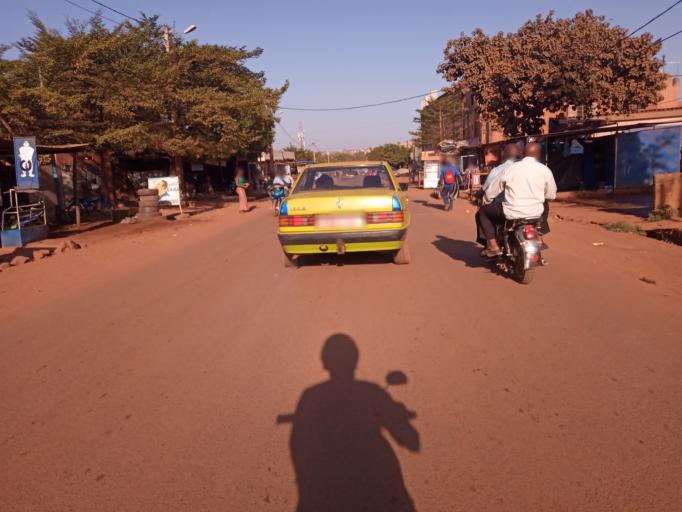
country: ML
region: Bamako
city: Bamako
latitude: 12.6129
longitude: -7.9524
